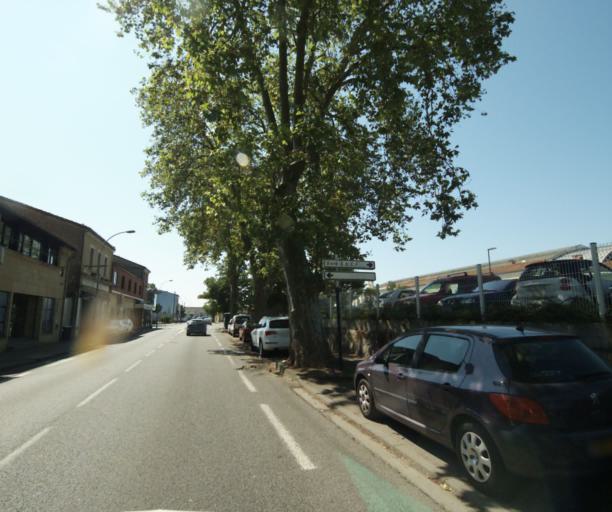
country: FR
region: Midi-Pyrenees
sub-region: Departement du Tarn-et-Garonne
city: Montauban
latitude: 44.0152
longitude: 1.3414
